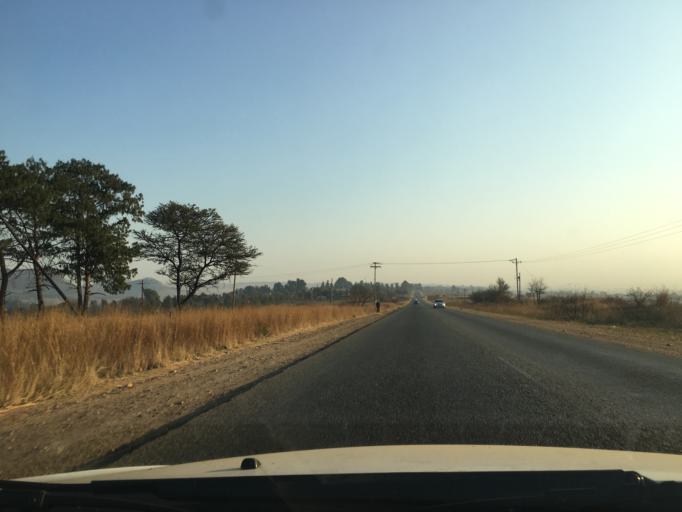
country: ZA
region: Gauteng
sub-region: West Rand District Municipality
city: Muldersdriseloop
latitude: -26.0089
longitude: 27.8583
